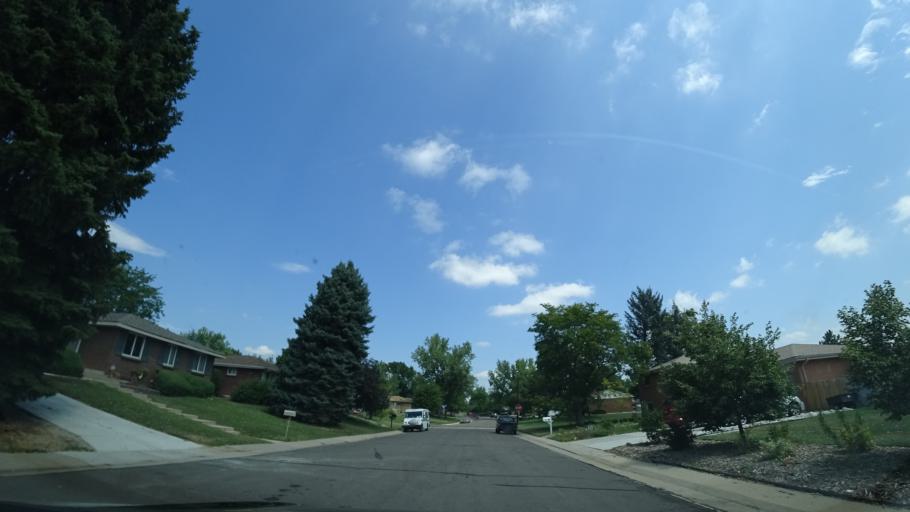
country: US
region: Colorado
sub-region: Jefferson County
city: Lakewood
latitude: 39.7161
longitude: -105.0740
